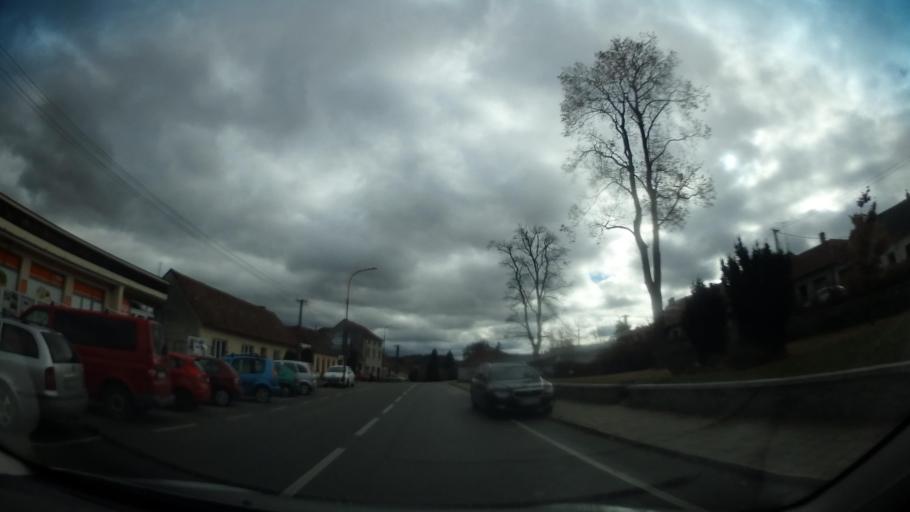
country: CZ
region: Vysocina
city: Budisov
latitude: 49.2877
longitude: 16.0958
